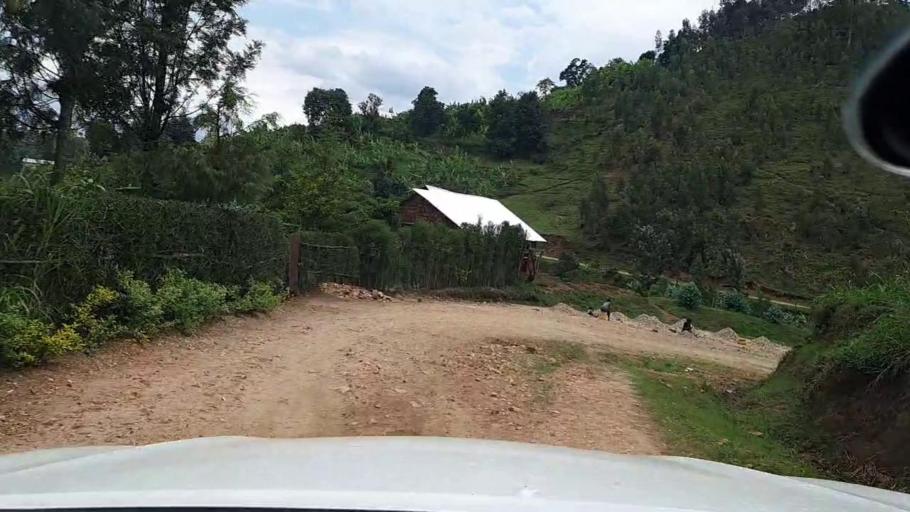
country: RW
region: Western Province
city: Kibuye
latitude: -2.0803
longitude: 29.4212
